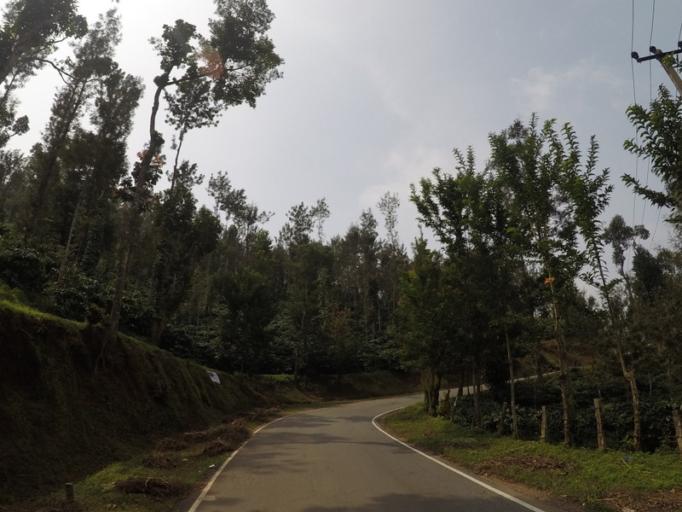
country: IN
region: Karnataka
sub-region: Chikmagalur
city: Mudigere
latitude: 13.1989
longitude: 75.4017
